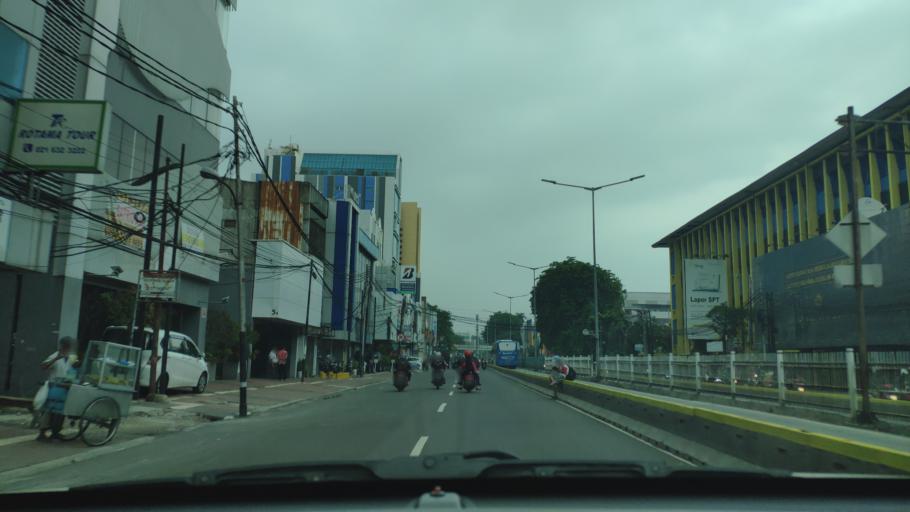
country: ID
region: Jakarta Raya
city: Jakarta
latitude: -6.1649
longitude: 106.8187
